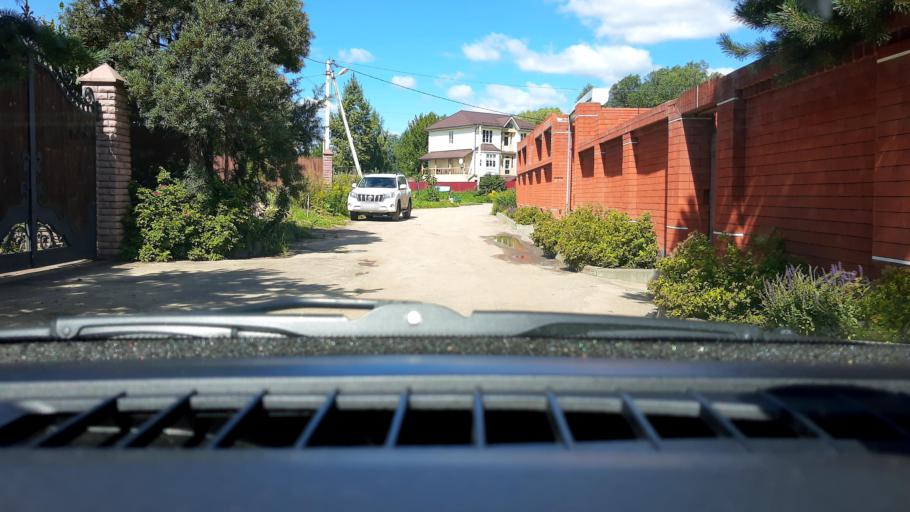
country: RU
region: Nizjnij Novgorod
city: Afonino
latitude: 56.2474
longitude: 44.0814
